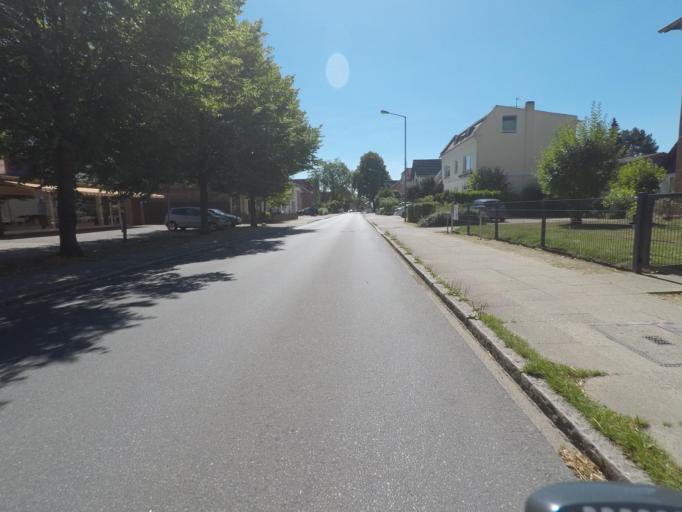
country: DE
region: Schleswig-Holstein
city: Trittau
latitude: 53.6172
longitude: 10.4028
